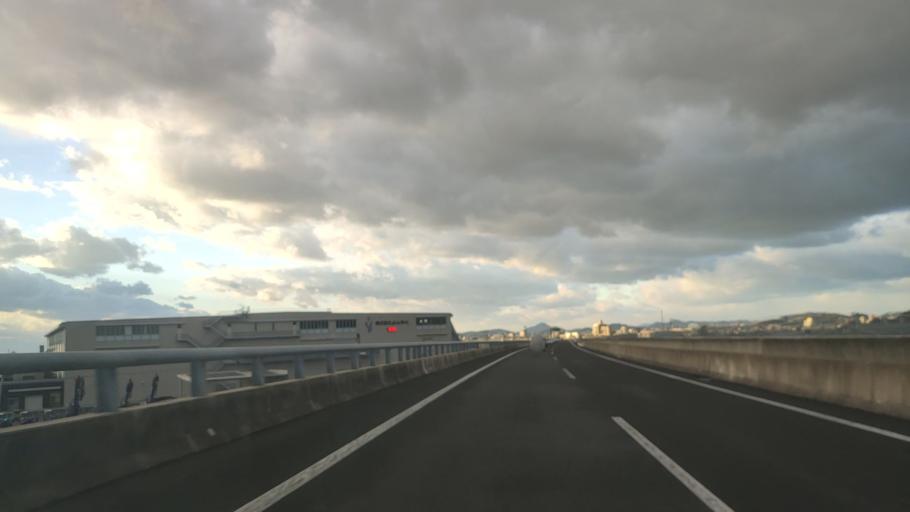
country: JP
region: Ehime
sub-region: Shikoku-chuo Shi
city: Matsuyama
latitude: 33.7896
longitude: 132.8057
